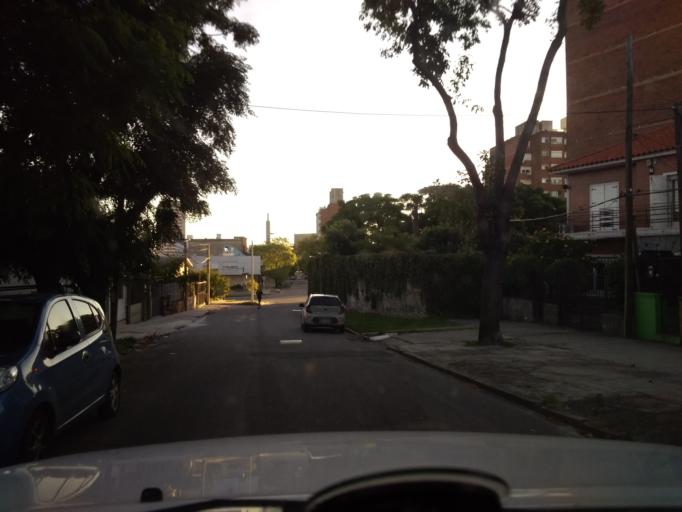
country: UY
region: Montevideo
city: Montevideo
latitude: -34.8911
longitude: -56.1451
